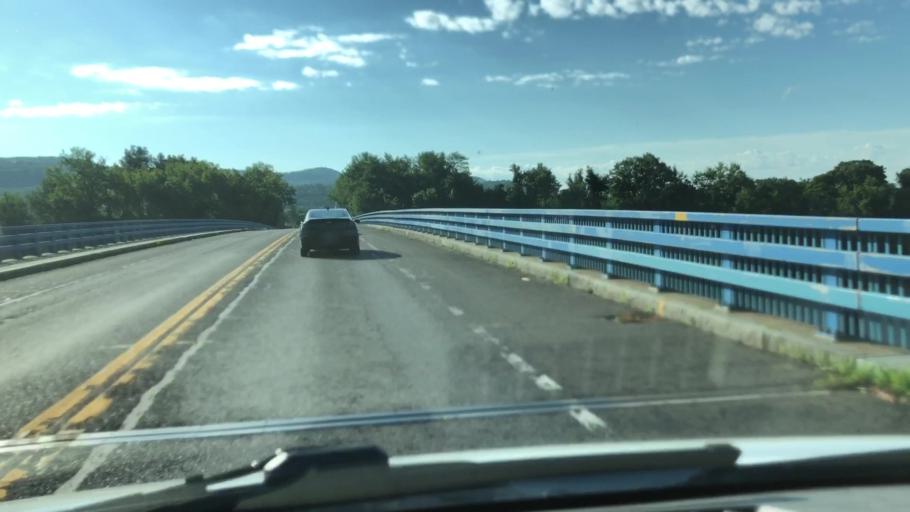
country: US
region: Massachusetts
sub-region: Franklin County
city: South Deerfield
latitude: 42.4680
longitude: -72.5859
